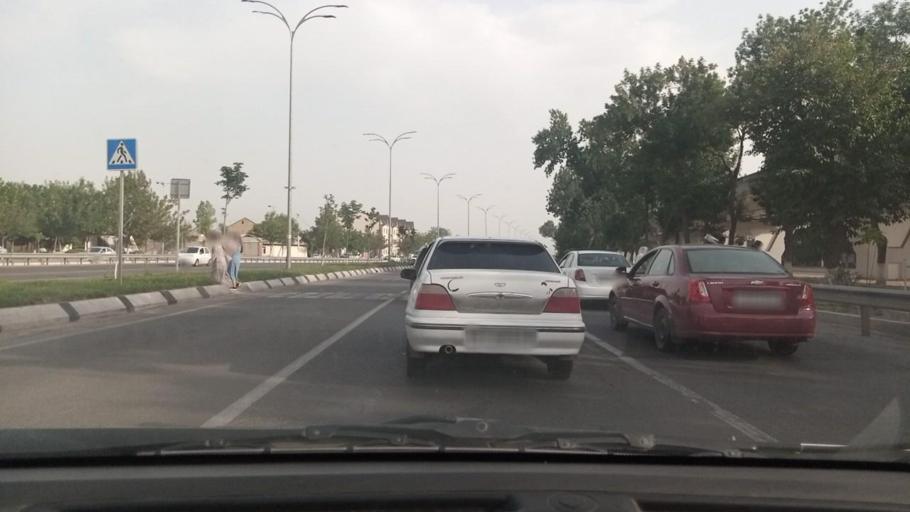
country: UZ
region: Toshkent Shahri
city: Bektemir
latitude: 41.2887
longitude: 69.3594
